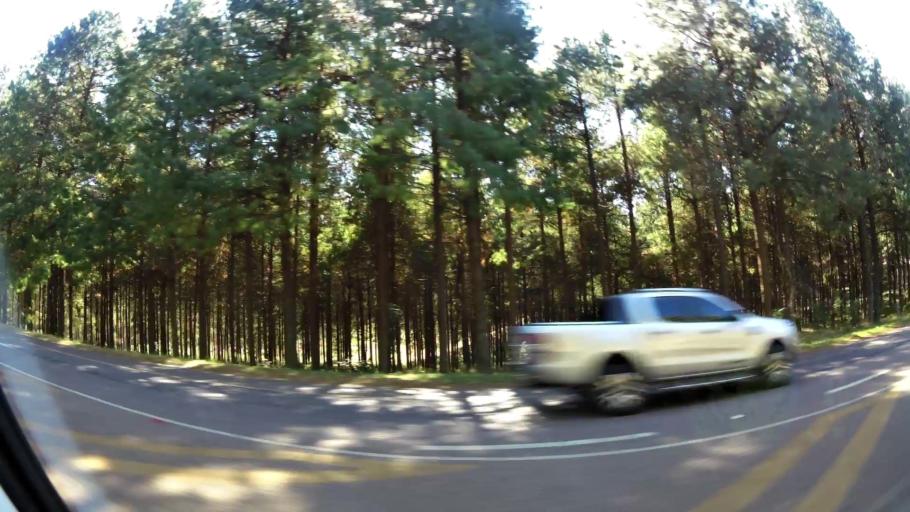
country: ZA
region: Limpopo
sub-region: Capricorn District Municipality
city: Mankoeng
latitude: -23.9275
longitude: 29.9601
